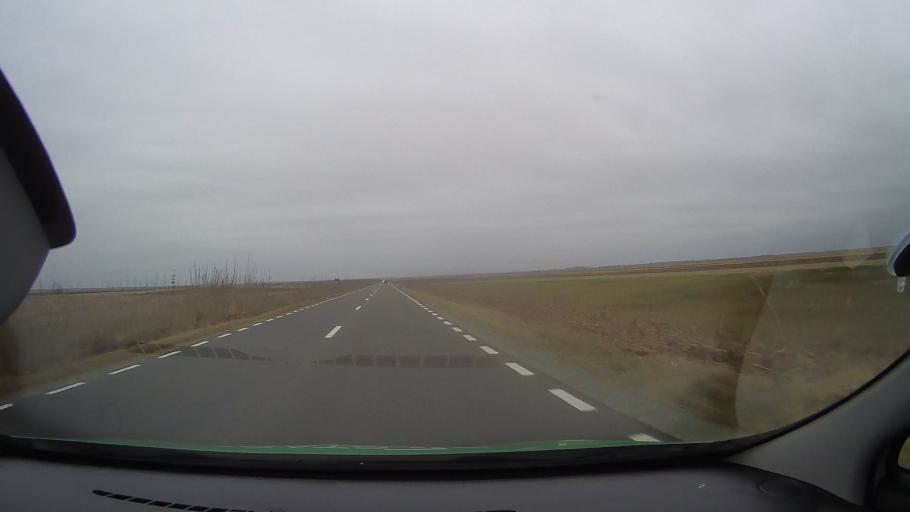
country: RO
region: Ialomita
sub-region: Comuna Gheorghe Lazar
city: Gheorghe Lazar
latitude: 44.6464
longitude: 27.4050
